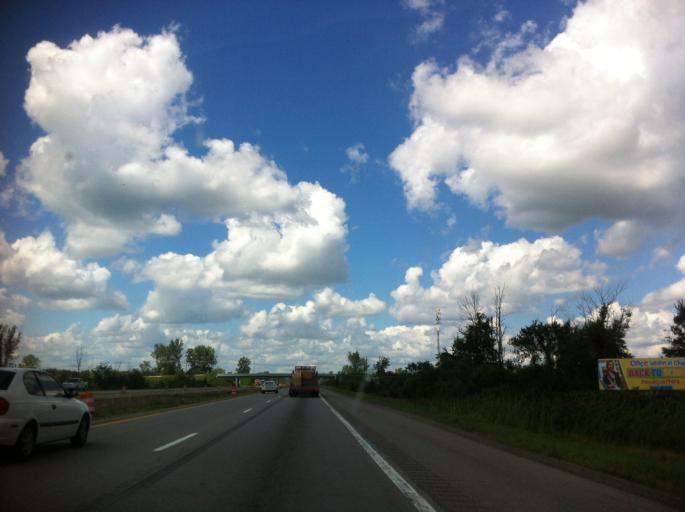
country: US
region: Michigan
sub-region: Washtenaw County
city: Milan
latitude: 42.1098
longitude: -83.6822
